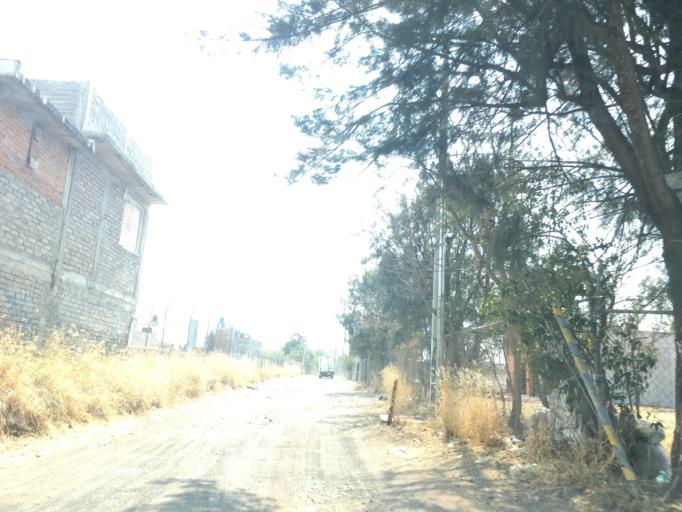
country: MX
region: Michoacan
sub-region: Morelia
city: Morelos
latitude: 19.6718
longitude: -101.2287
